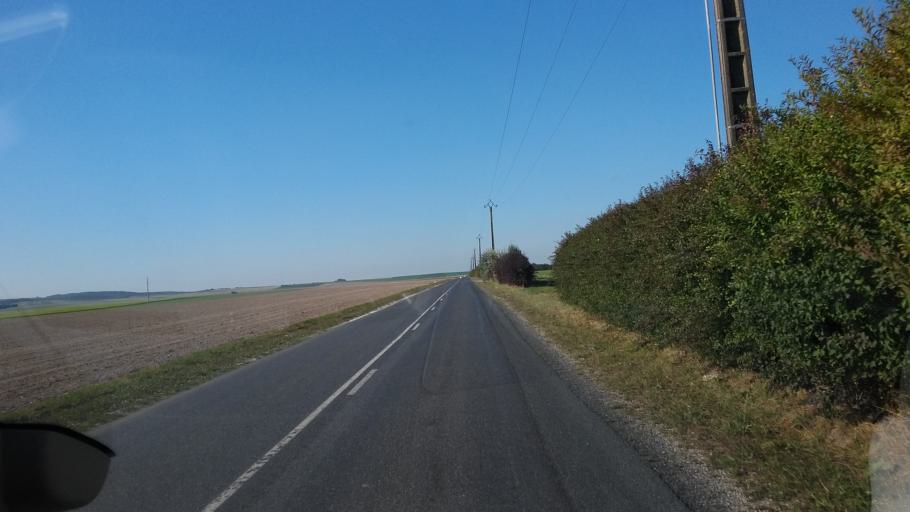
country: FR
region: Champagne-Ardenne
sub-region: Departement de la Marne
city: Connantre
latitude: 48.7330
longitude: 3.9051
